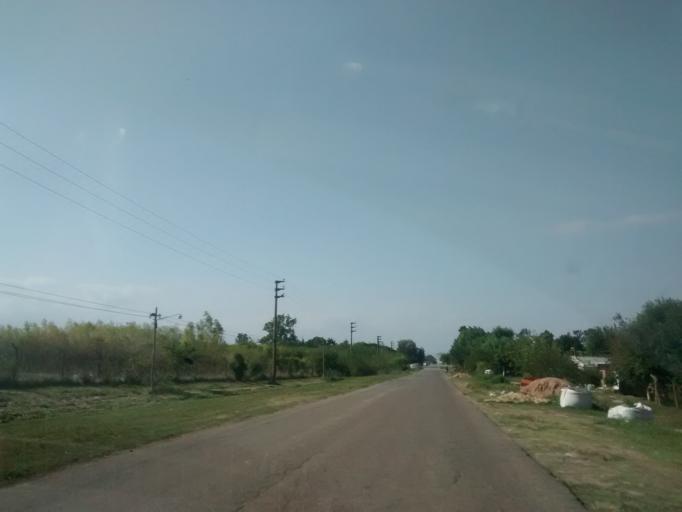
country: AR
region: Buenos Aires
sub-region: Partido de La Plata
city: La Plata
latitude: -34.9988
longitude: -57.8947
